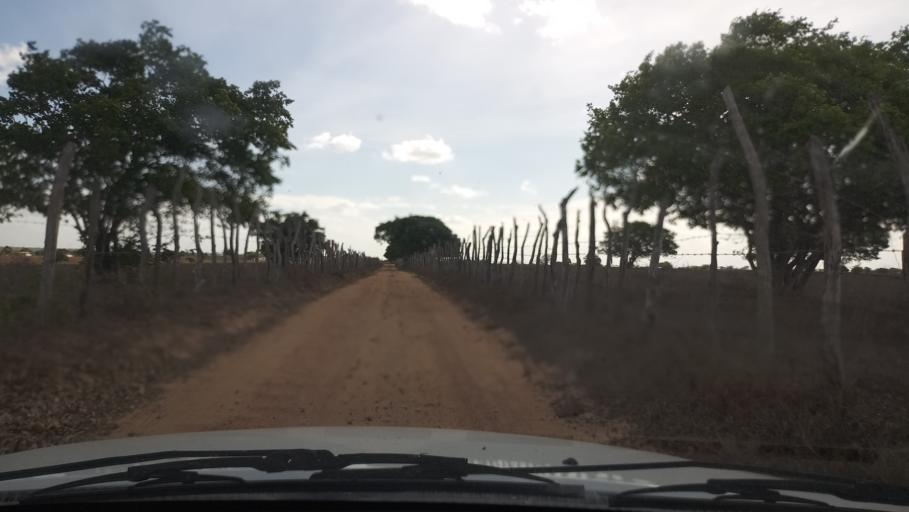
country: BR
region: Rio Grande do Norte
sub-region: Goianinha
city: Goianinha
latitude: -6.3053
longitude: -35.3038
